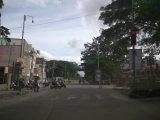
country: IN
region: Karnataka
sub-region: Bangalore Urban
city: Bangalore
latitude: 12.9903
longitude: 77.5507
